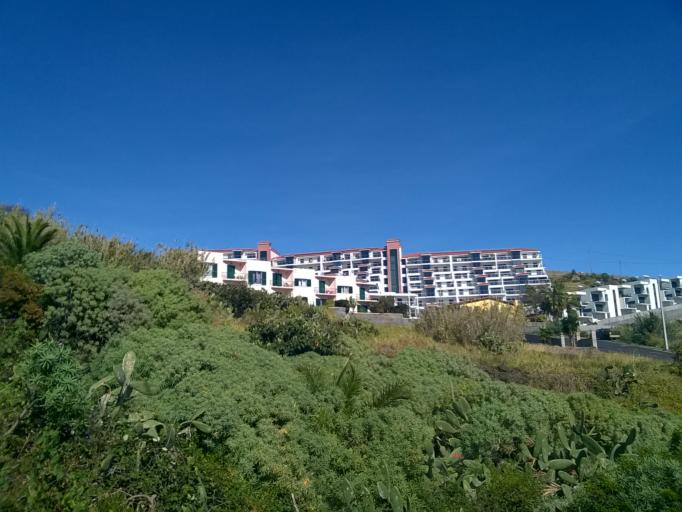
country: PT
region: Madeira
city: Canico
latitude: 32.6446
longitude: -16.8342
